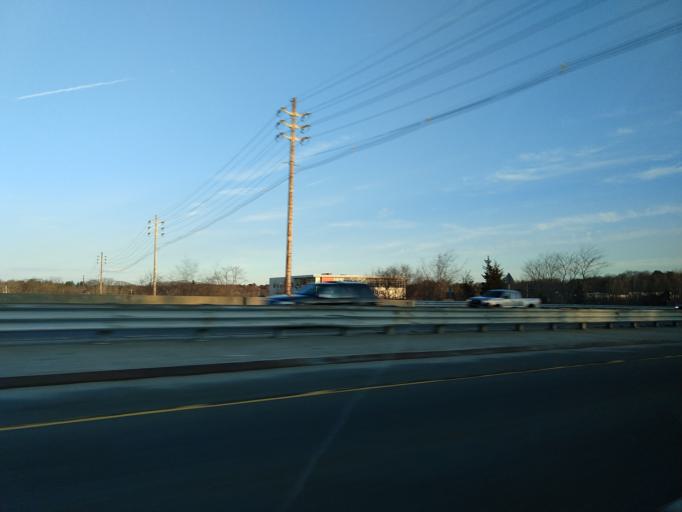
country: US
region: Massachusetts
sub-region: Essex County
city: South Peabody
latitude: 42.5420
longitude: -70.9839
